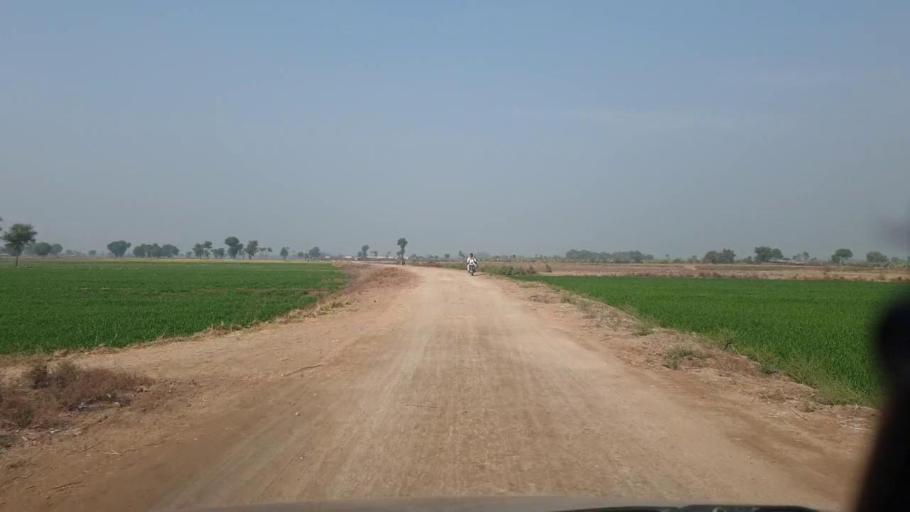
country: PK
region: Sindh
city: Shahdadpur
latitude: 26.0349
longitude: 68.5037
